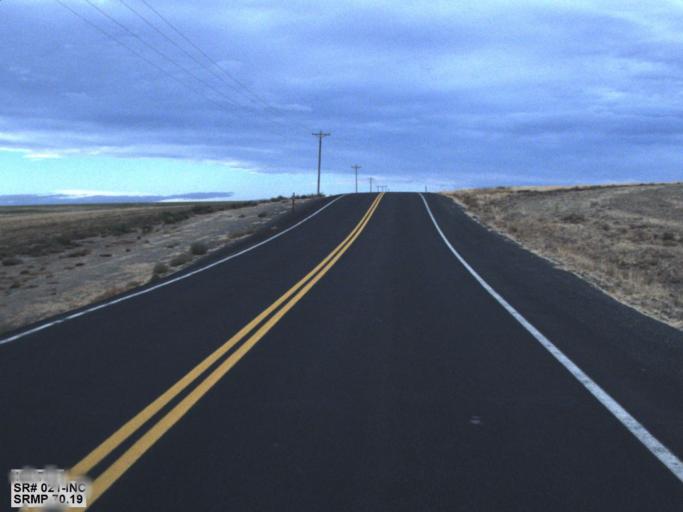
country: US
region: Washington
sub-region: Okanogan County
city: Coulee Dam
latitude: 47.4983
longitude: -118.7849
